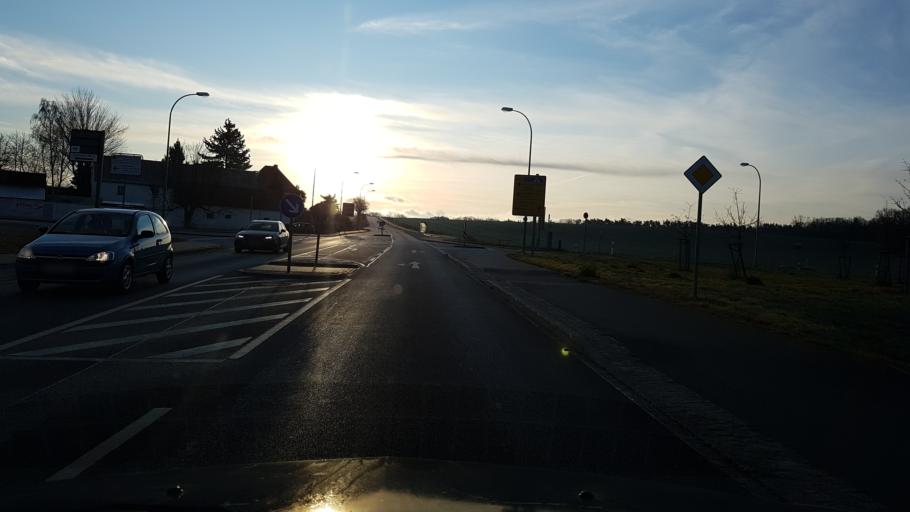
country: DE
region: Saxony
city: Radibor
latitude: 51.2362
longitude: 14.3709
